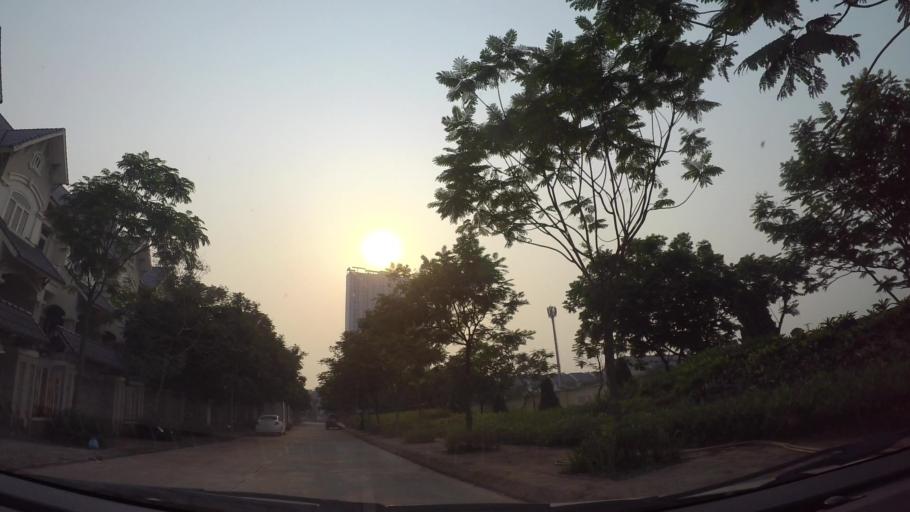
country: VN
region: Ha Noi
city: Cau Dien
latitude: 21.0082
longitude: 105.7340
